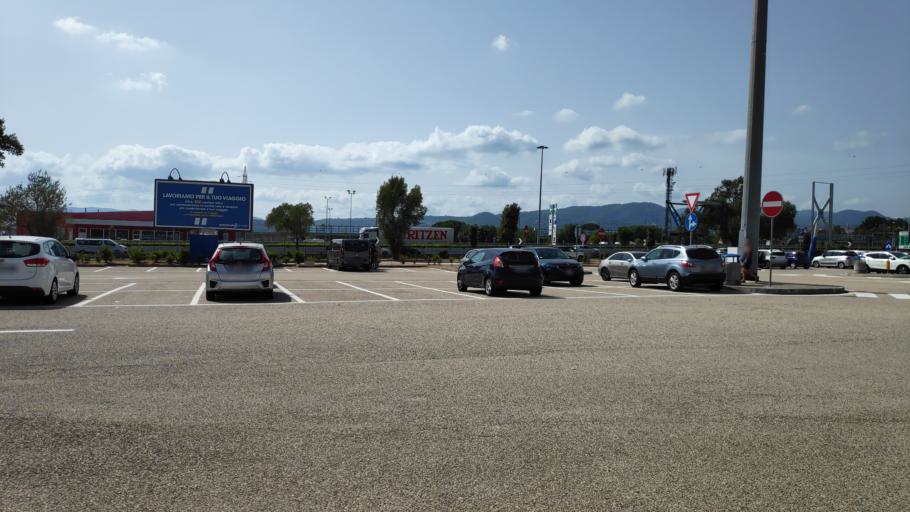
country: IT
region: Campania
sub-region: Provincia di Caserta
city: Teano
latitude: 41.2338
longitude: 14.0940
